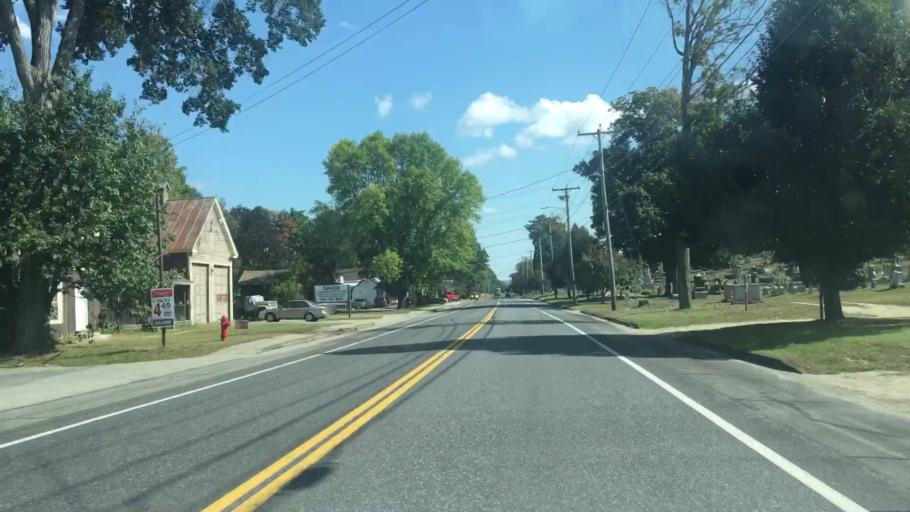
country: US
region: Maine
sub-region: Franklin County
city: Farmington
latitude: 44.6598
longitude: -70.1444
